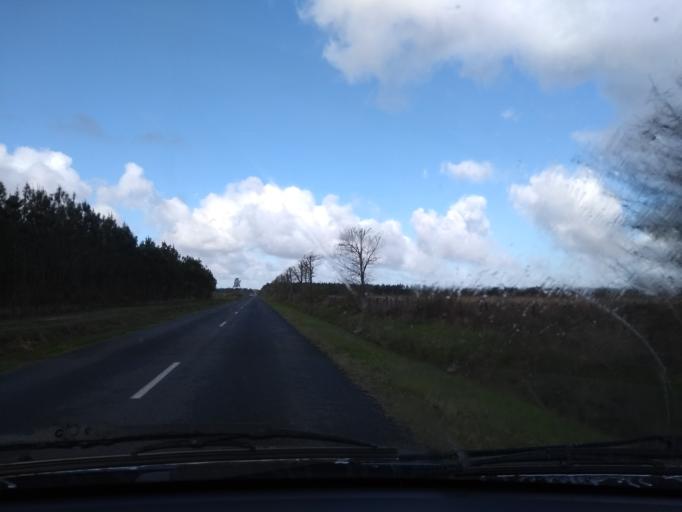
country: FR
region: Aquitaine
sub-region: Departement de la Gironde
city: Mios
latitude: 44.5506
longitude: -0.9591
